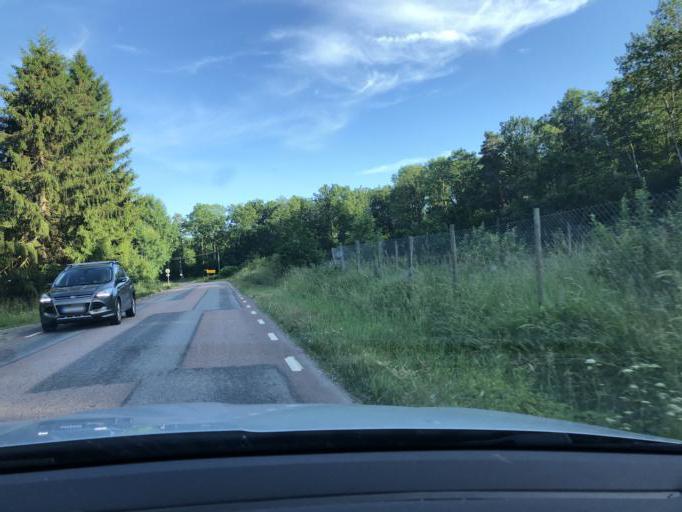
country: SE
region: Blekinge
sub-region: Solvesborgs Kommun
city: Soelvesborg
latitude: 56.1439
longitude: 14.6052
